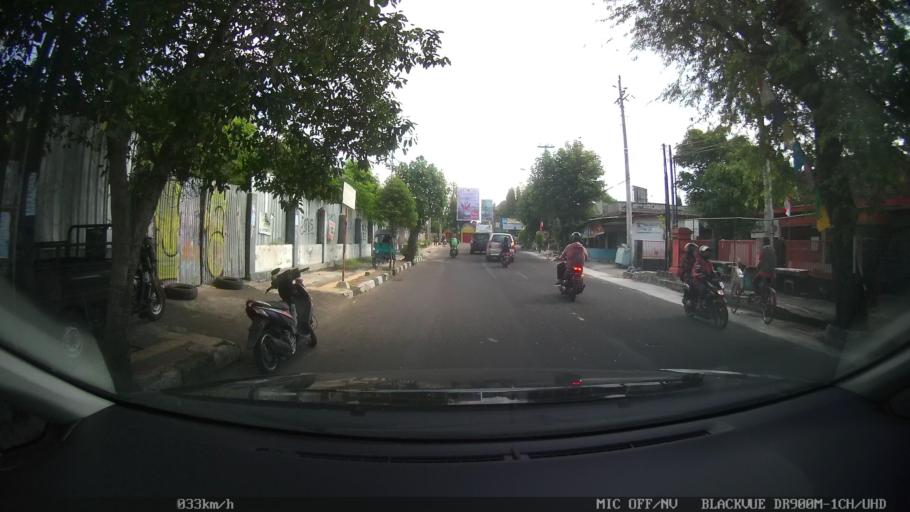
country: ID
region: Daerah Istimewa Yogyakarta
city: Yogyakarta
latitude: -7.8162
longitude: 110.3732
